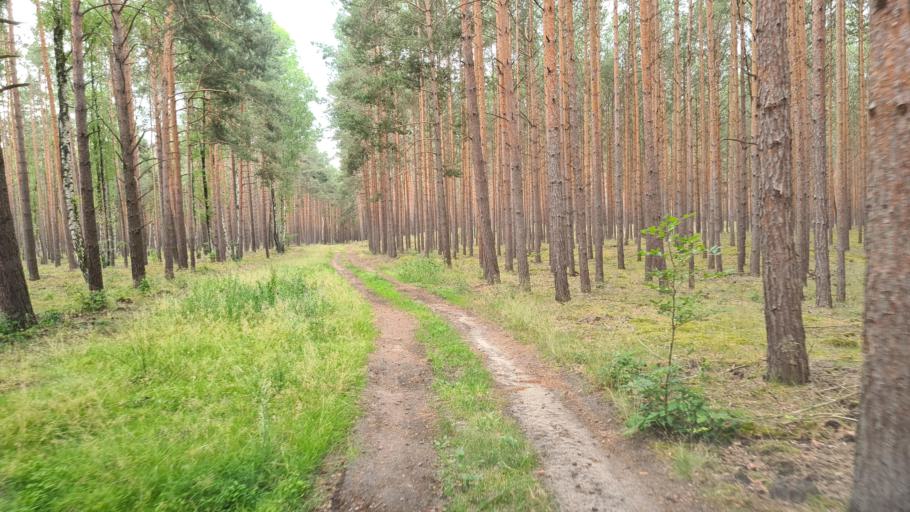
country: DE
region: Brandenburg
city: Crinitz
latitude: 51.7322
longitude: 13.7189
